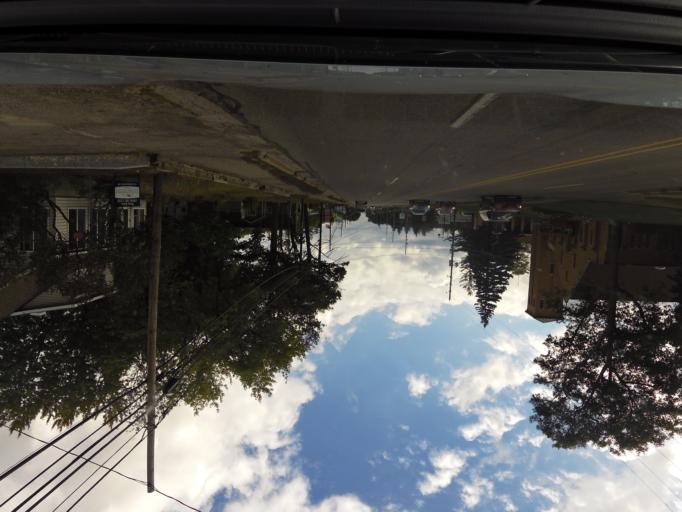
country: US
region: Michigan
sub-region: Roscommon County
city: Prudenville
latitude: 44.2985
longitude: -84.6568
